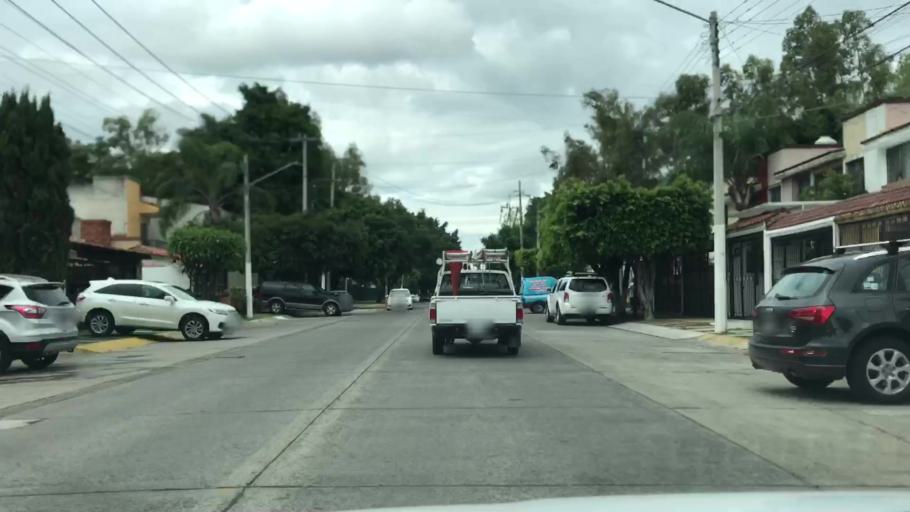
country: MX
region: Jalisco
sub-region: Tlajomulco de Zuniga
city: Palomar
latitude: 20.6372
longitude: -103.4371
